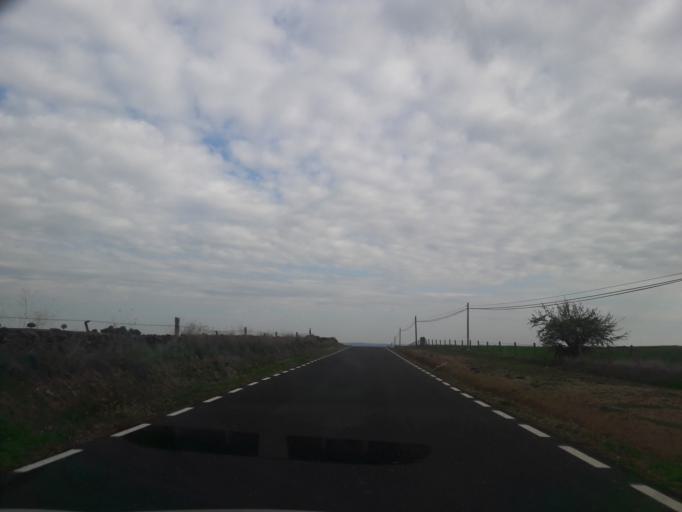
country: ES
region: Castille and Leon
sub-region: Provincia de Salamanca
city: Pastores
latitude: 40.5046
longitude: -6.5296
